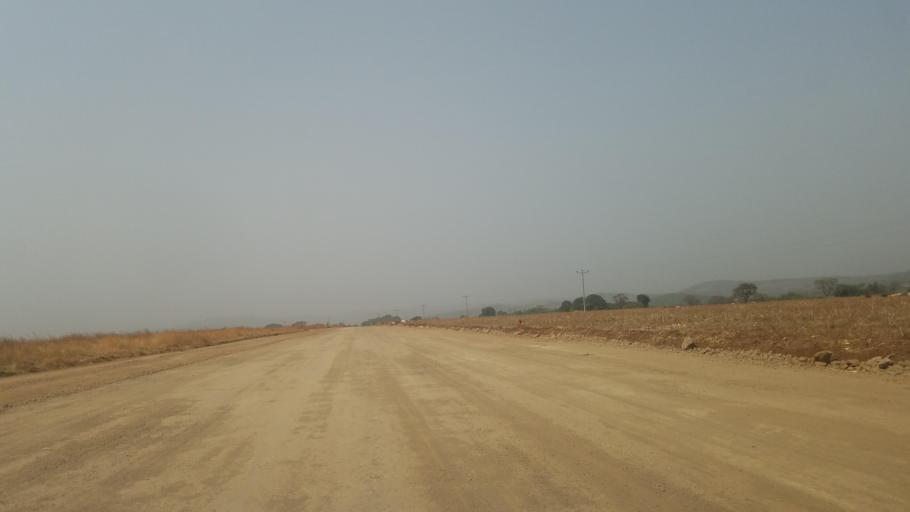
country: ET
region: Amhara
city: Bure
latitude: 10.8953
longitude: 36.4574
